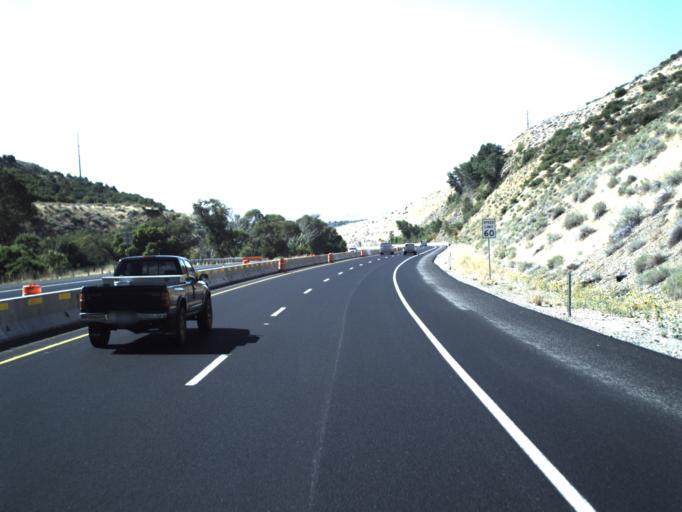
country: US
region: Utah
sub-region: Box Elder County
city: Brigham City
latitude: 41.4982
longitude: -111.9785
